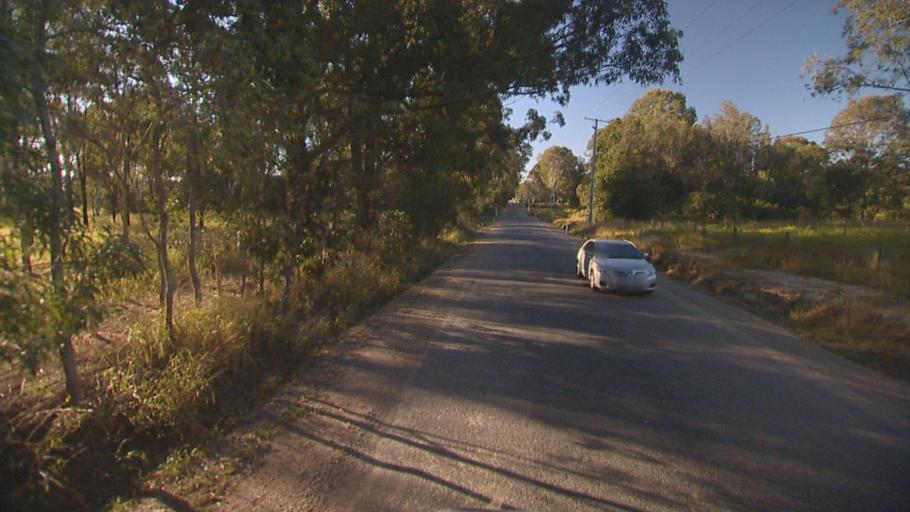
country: AU
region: Queensland
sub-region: Logan
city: Logan Reserve
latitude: -27.7600
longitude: 153.1396
